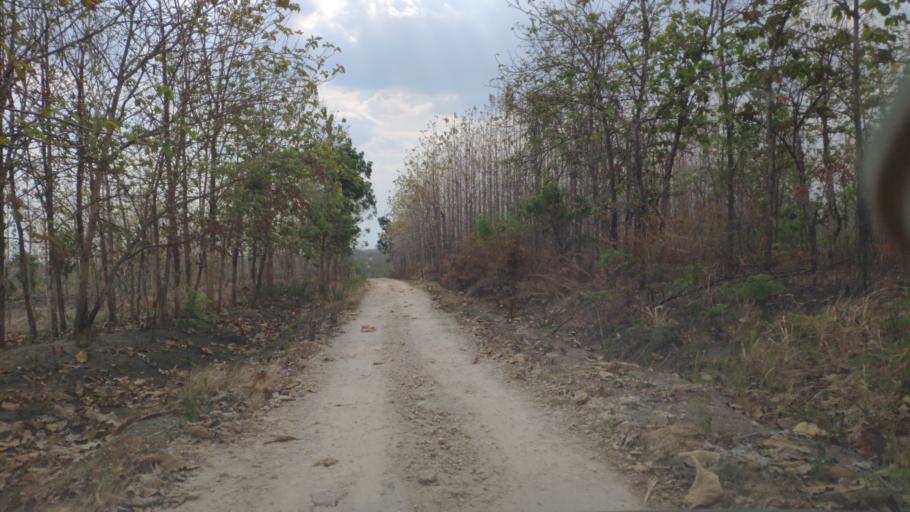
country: ID
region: Central Java
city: Randublatung
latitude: -7.3035
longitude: 111.3467
